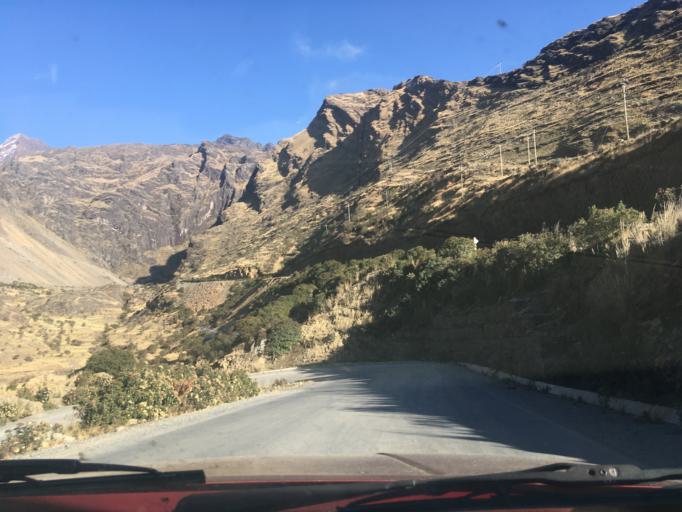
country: BO
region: La Paz
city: Quime
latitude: -17.0035
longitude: -67.2684
